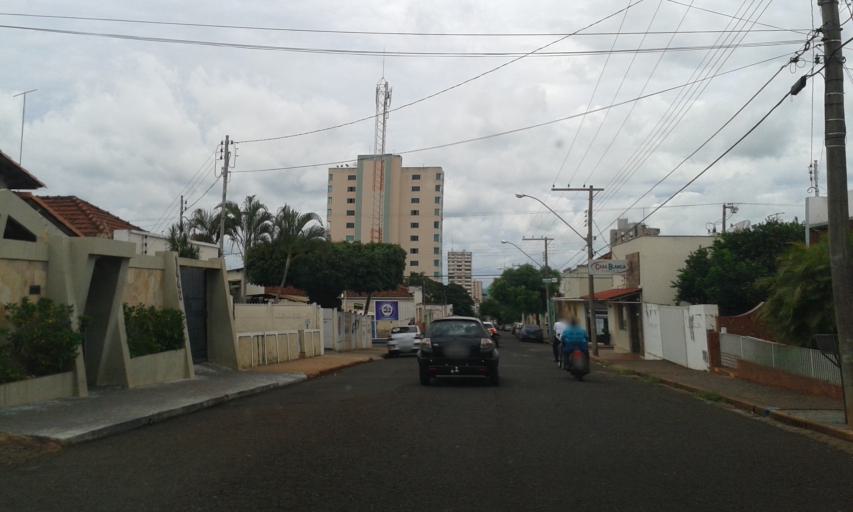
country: BR
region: Minas Gerais
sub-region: Ituiutaba
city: Ituiutaba
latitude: -18.9800
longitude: -49.4608
